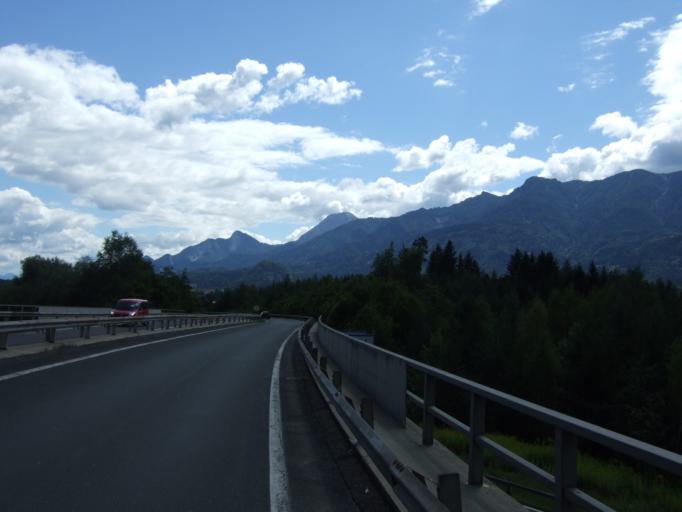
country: AT
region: Carinthia
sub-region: Politischer Bezirk Villach Land
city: Finkenstein am Faaker See
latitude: 46.5723
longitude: 13.8257
